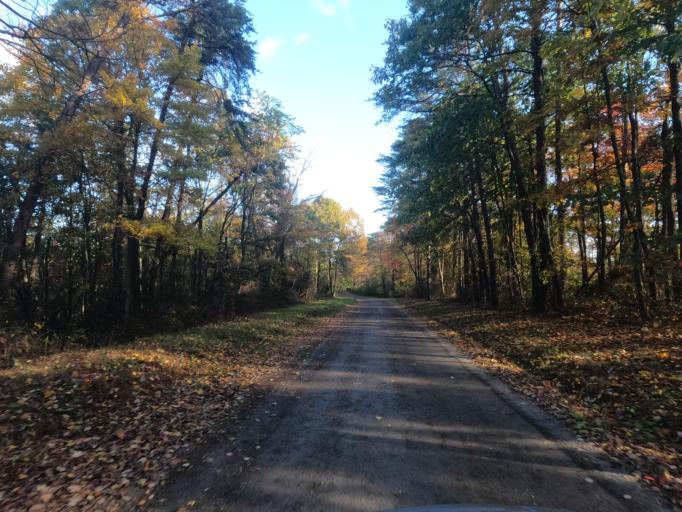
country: US
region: West Virginia
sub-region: Morgan County
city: Berkeley Springs
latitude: 39.6093
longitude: -78.4935
